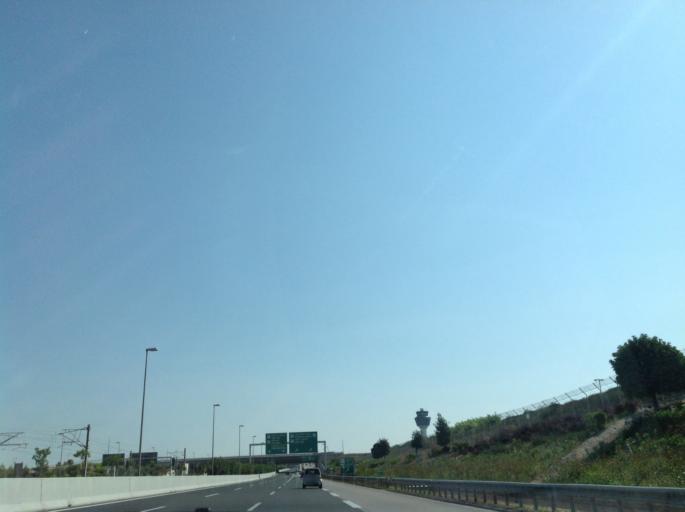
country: GR
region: Attica
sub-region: Nomarchia Anatolikis Attikis
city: Spata
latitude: 37.9280
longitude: 23.9367
